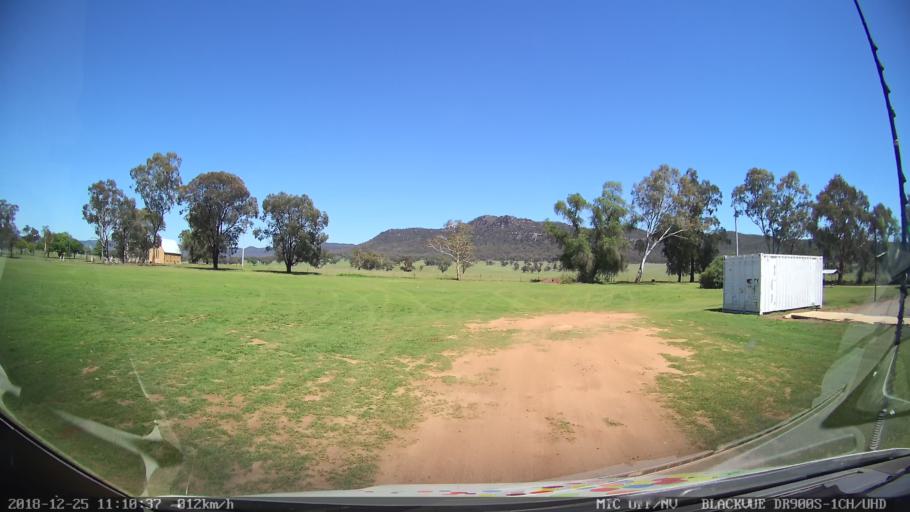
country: AU
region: New South Wales
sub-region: Upper Hunter Shire
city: Merriwa
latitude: -32.4162
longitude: 150.1141
